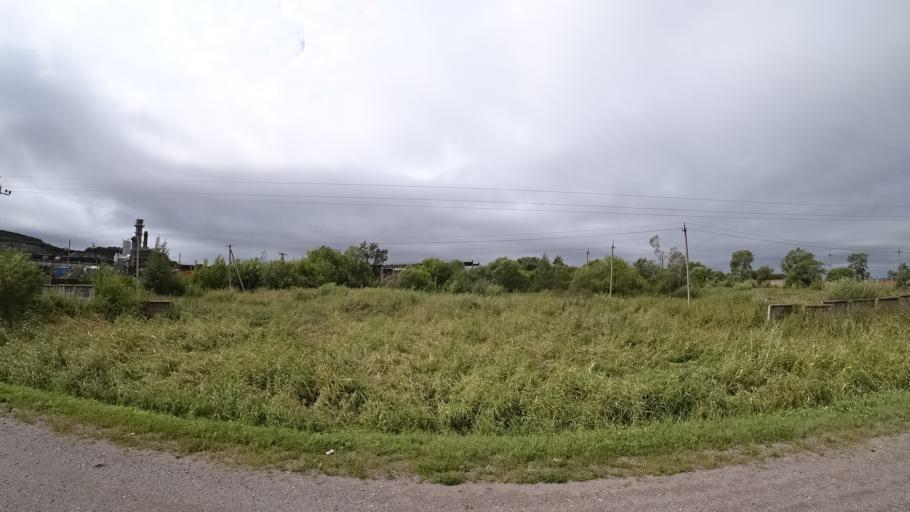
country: RU
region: Primorskiy
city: Monastyrishche
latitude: 44.1703
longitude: 132.4410
